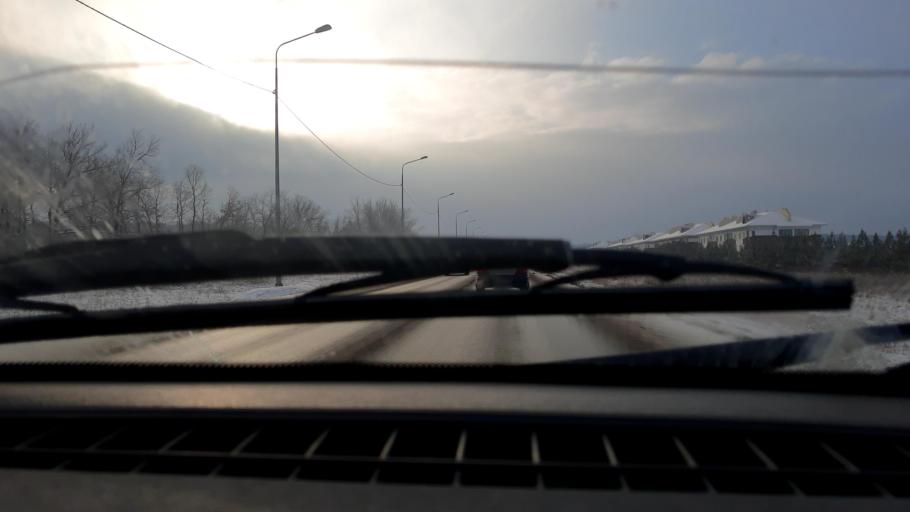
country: RU
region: Bashkortostan
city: Avdon
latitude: 54.4824
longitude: 55.8881
